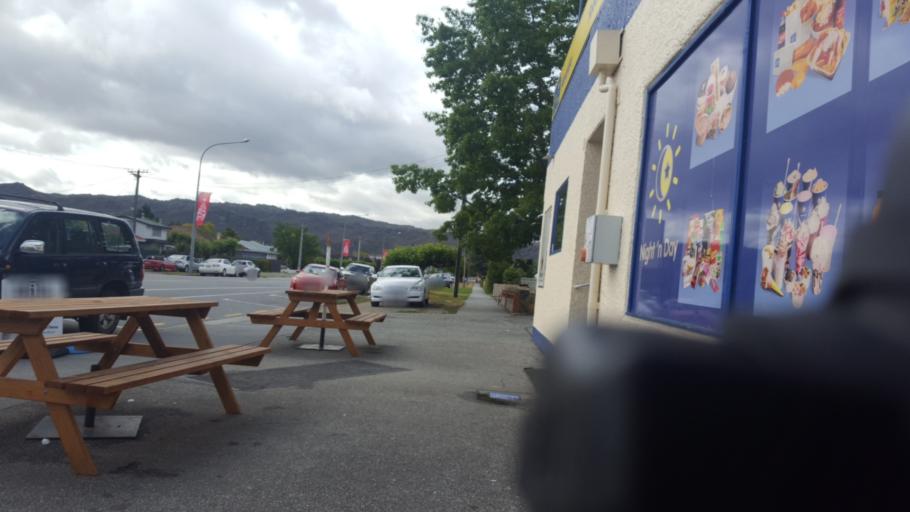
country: NZ
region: Otago
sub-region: Queenstown-Lakes District
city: Wanaka
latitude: -45.2481
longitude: 169.3843
